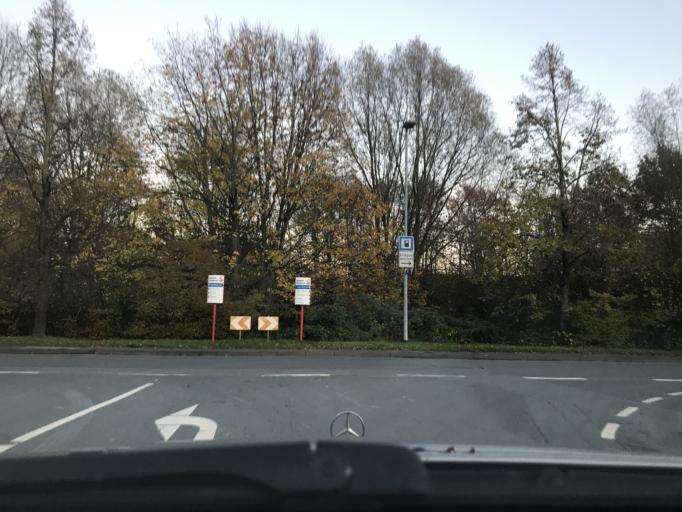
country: DE
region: North Rhine-Westphalia
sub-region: Regierungsbezirk Arnsberg
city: Soest
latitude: 51.5583
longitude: 8.1358
